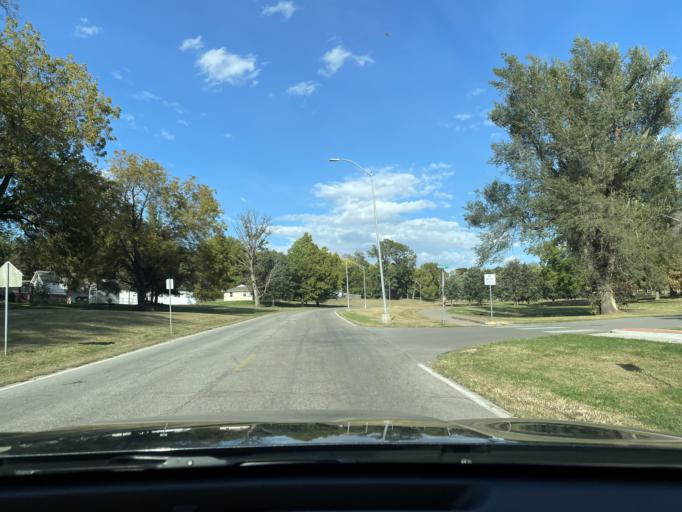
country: US
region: Kansas
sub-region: Doniphan County
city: Elwood
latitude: 39.7171
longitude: -94.8550
